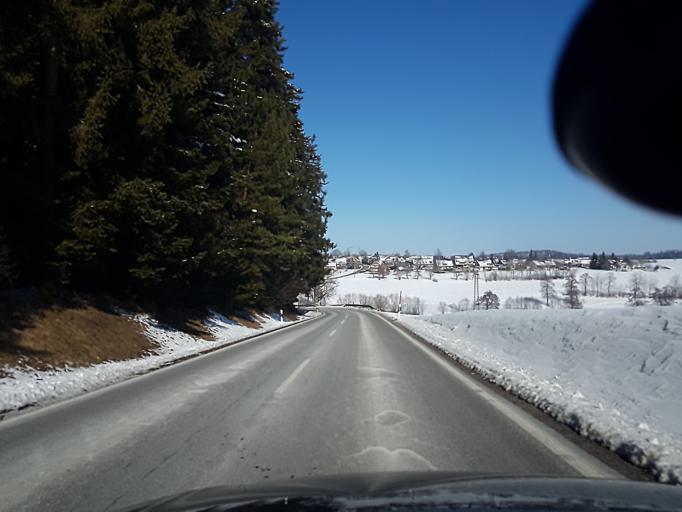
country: DE
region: Baden-Wuerttemberg
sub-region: Freiburg Region
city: Hardt
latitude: 48.1655
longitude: 8.4571
